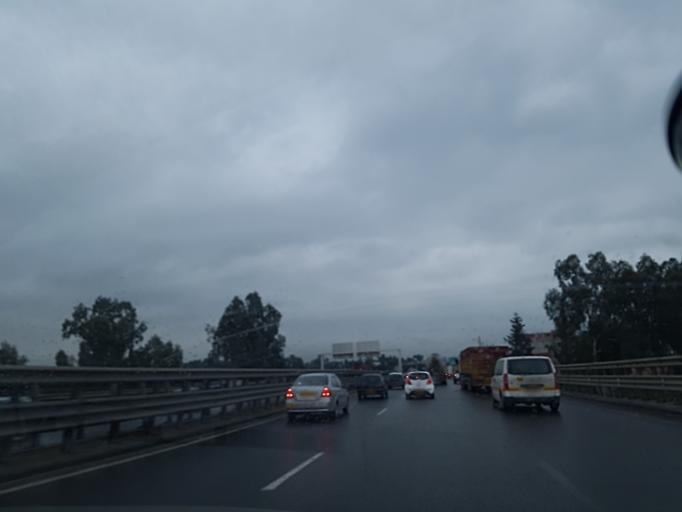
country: DZ
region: Boumerdes
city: Khemis el Khechna
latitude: 36.6733
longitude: 3.2933
